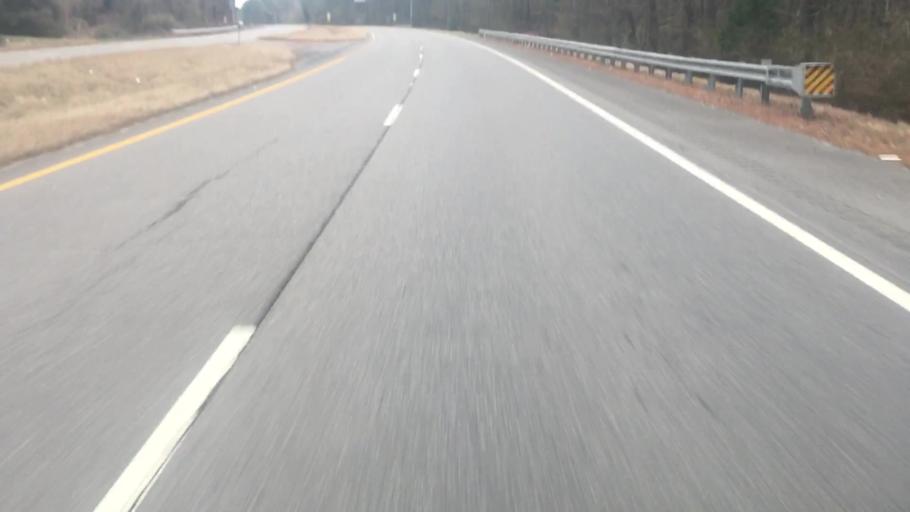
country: US
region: Alabama
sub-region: Walker County
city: Cordova
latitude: 33.8216
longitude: -87.1870
